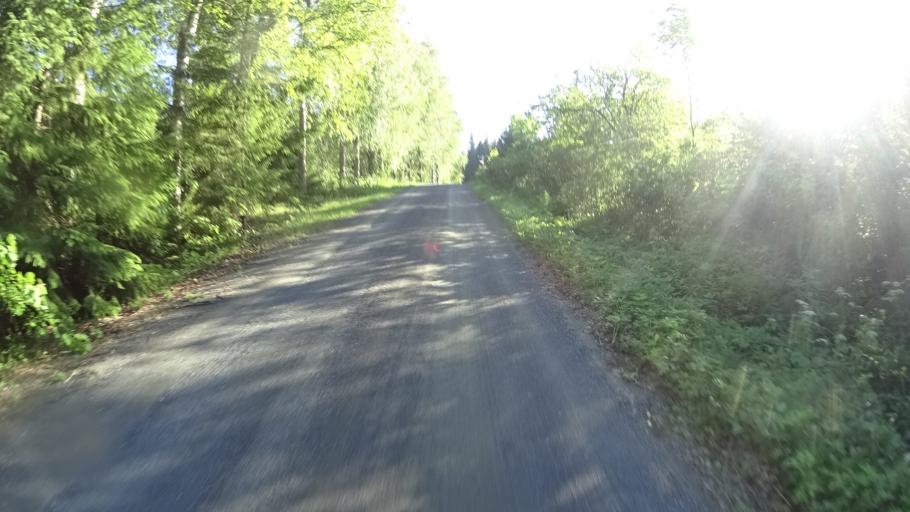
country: FI
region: Uusimaa
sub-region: Helsinki
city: Karkkila
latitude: 60.6445
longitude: 24.1204
